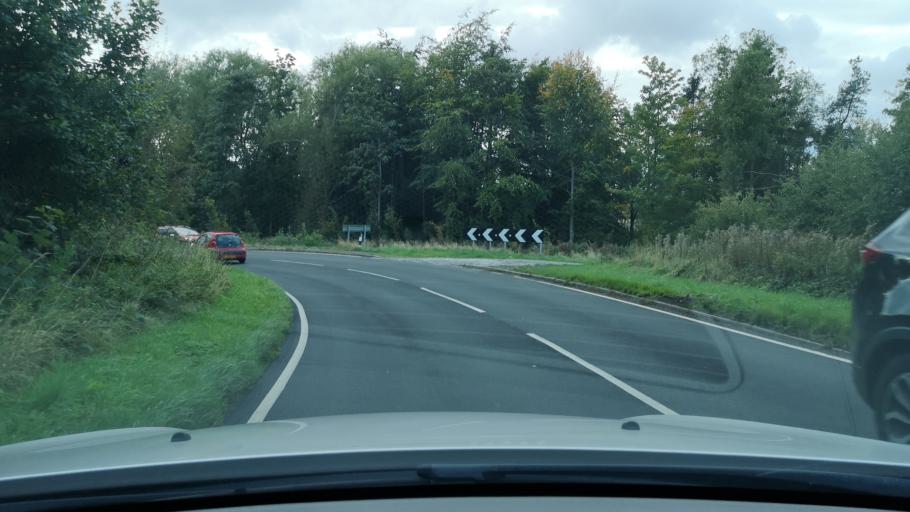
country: GB
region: England
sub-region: East Riding of Yorkshire
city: Hotham
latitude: 53.7865
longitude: -0.6351
